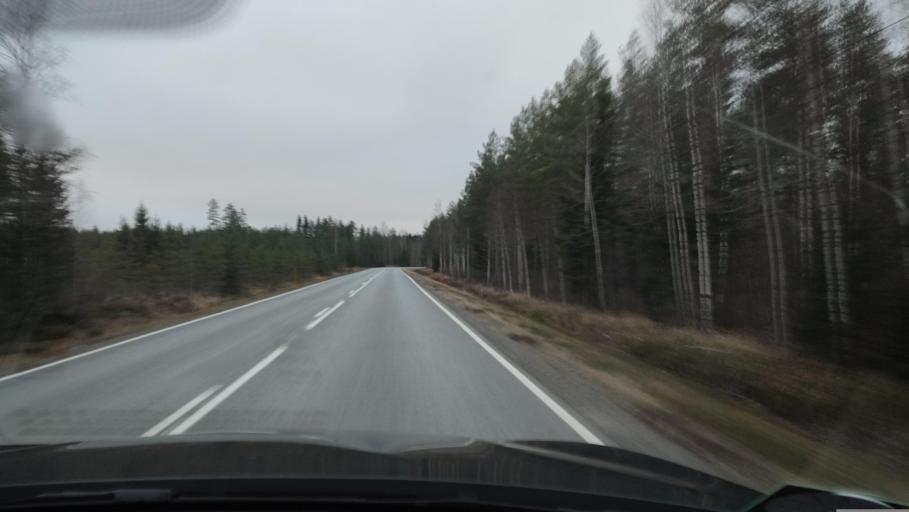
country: FI
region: Southern Ostrobothnia
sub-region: Suupohja
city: Karijoki
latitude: 62.3253
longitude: 21.8920
